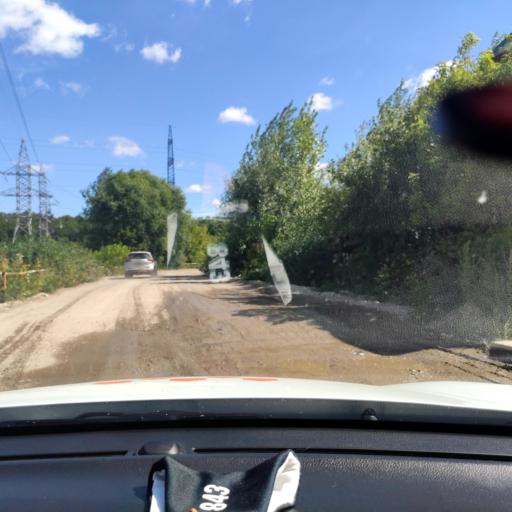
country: RU
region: Tatarstan
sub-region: Gorod Kazan'
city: Kazan
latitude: 55.8240
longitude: 49.2028
